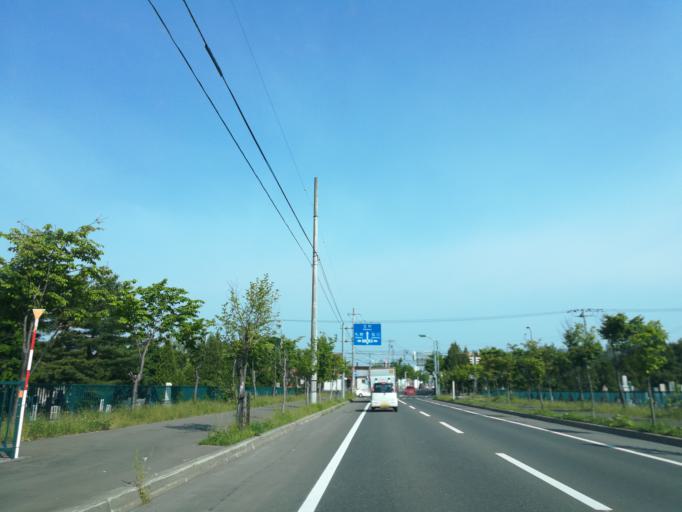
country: JP
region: Hokkaido
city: Iwamizawa
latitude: 43.2049
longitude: 141.7796
